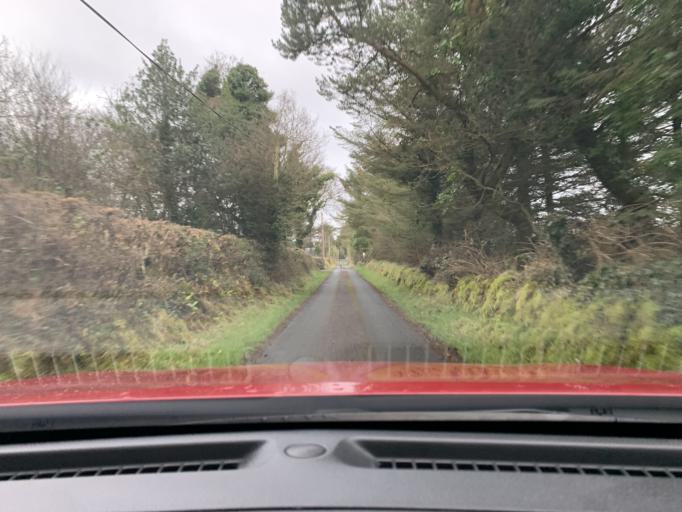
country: IE
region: Connaught
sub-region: Roscommon
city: Ballaghaderreen
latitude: 53.9660
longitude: -8.5126
